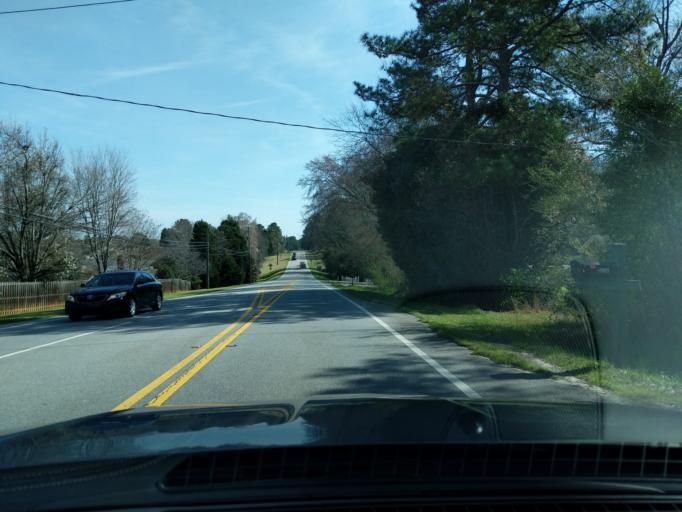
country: US
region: Georgia
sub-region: Columbia County
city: Evans
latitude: 33.5306
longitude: -82.1481
